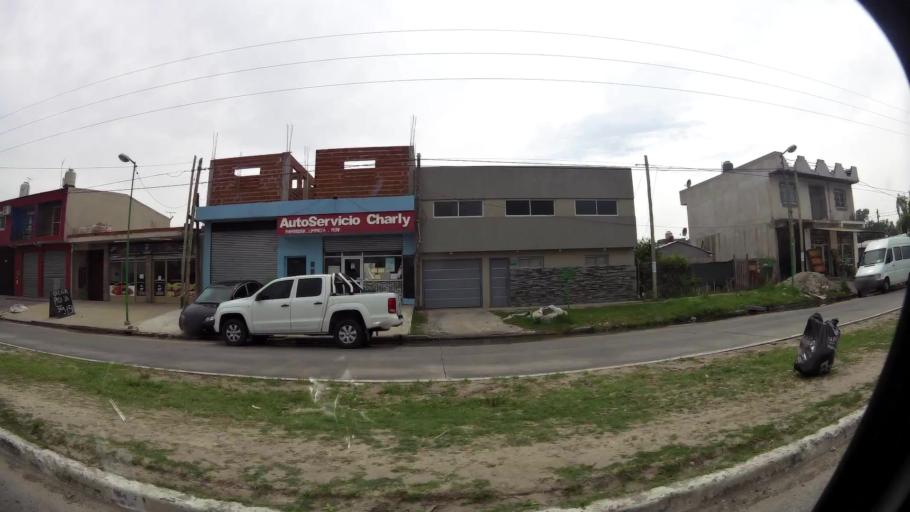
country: AR
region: Buenos Aires
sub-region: Partido de La Plata
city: La Plata
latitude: -34.9302
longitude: -58.0124
